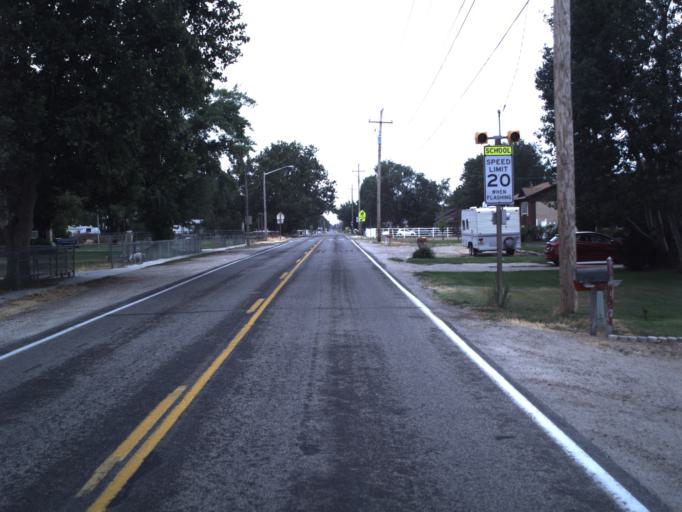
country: US
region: Utah
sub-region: Davis County
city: West Point
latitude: 41.1227
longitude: -112.1126
